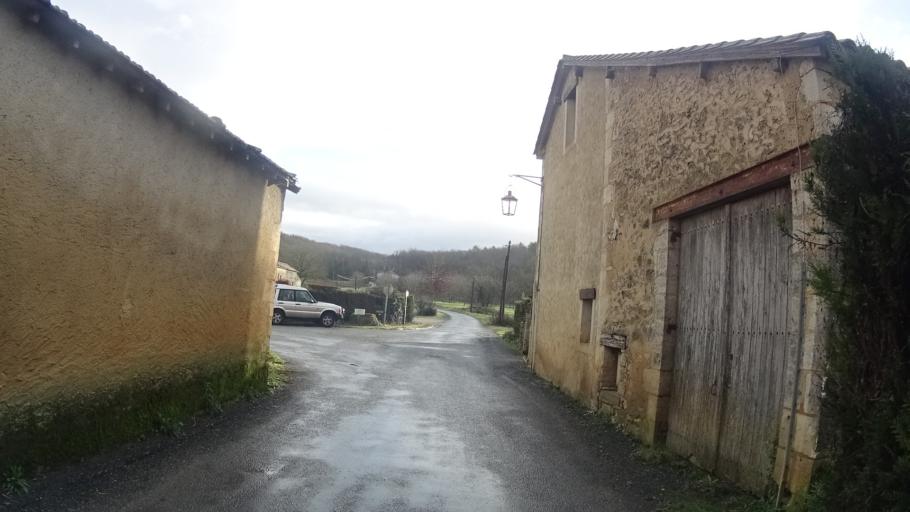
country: FR
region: Aquitaine
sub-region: Departement de la Dordogne
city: Sorges
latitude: 45.2450
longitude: 0.8968
